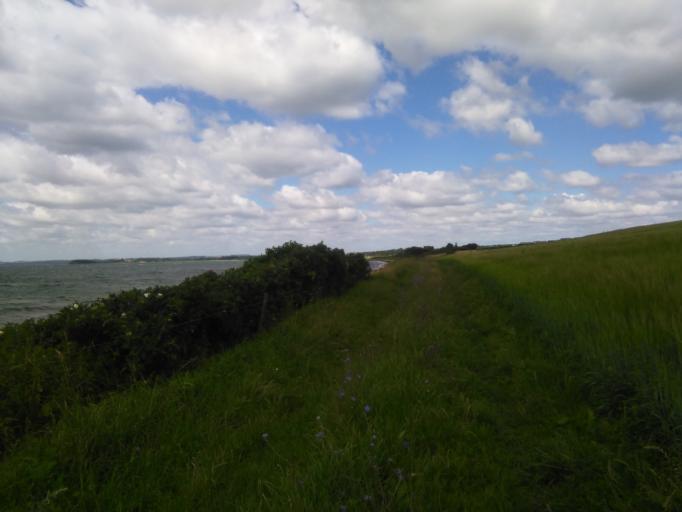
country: DK
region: Central Jutland
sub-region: Arhus Kommune
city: Logten
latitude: 56.1711
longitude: 10.3786
